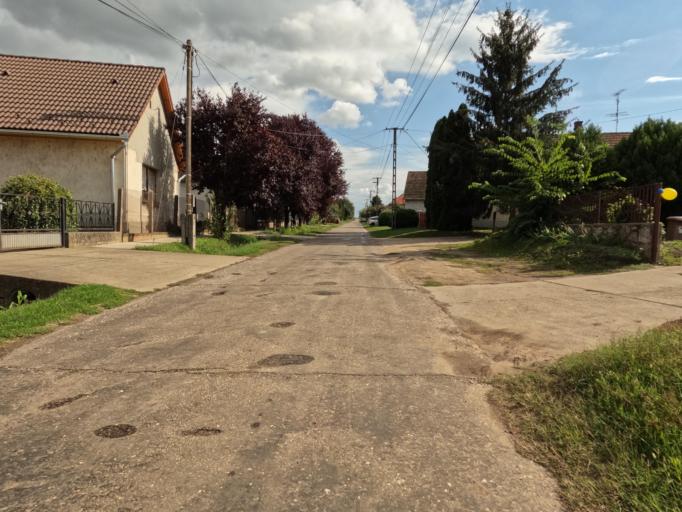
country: HU
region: Tolna
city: Tengelic
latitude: 46.5274
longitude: 18.7152
